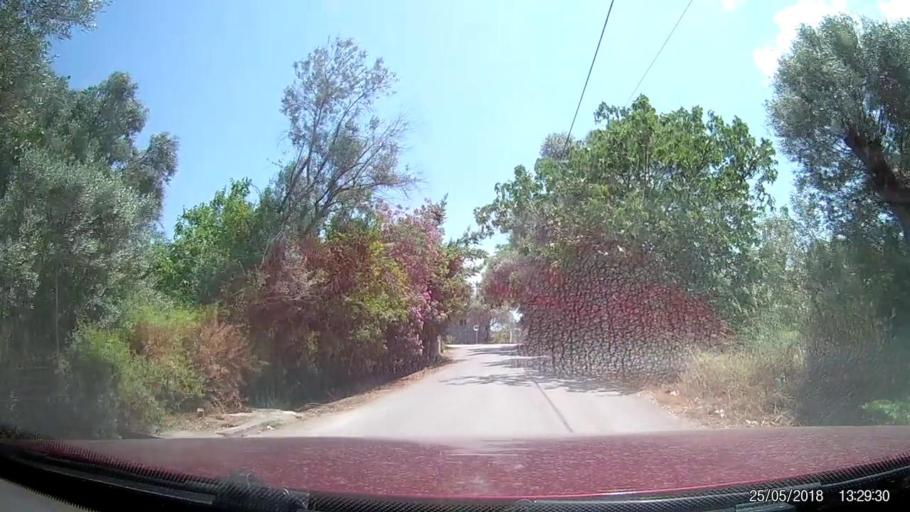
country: GR
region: Central Greece
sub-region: Nomos Evvoias
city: Mytikas
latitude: 38.4429
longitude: 23.6588
